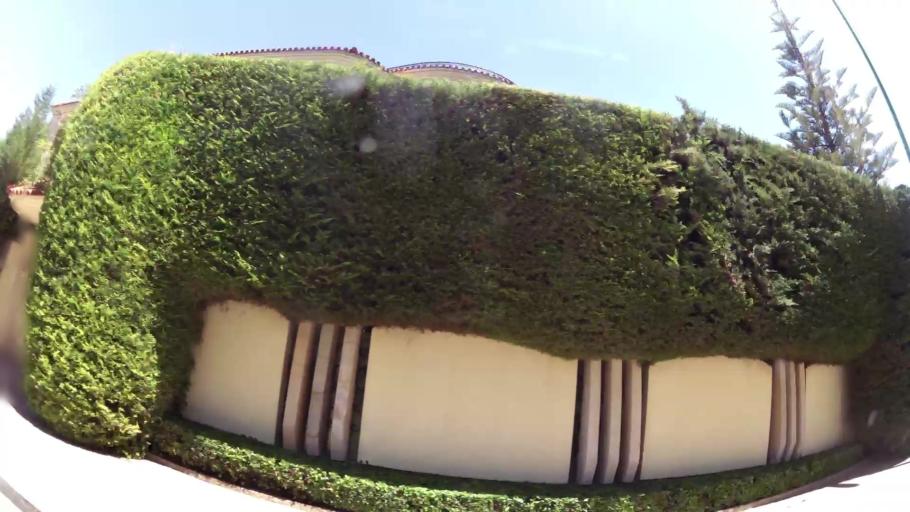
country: MA
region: Meknes-Tafilalet
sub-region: Meknes
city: Meknes
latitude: 33.9055
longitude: -5.5619
